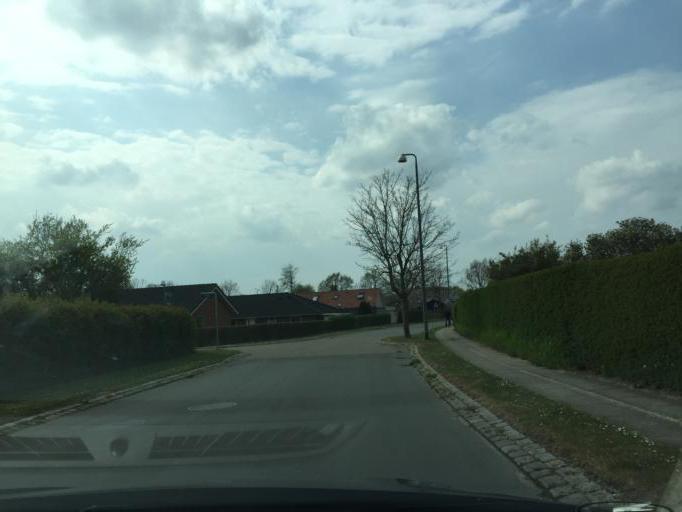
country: DK
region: South Denmark
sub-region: Odense Kommune
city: Neder Holluf
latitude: 55.3734
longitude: 10.4698
